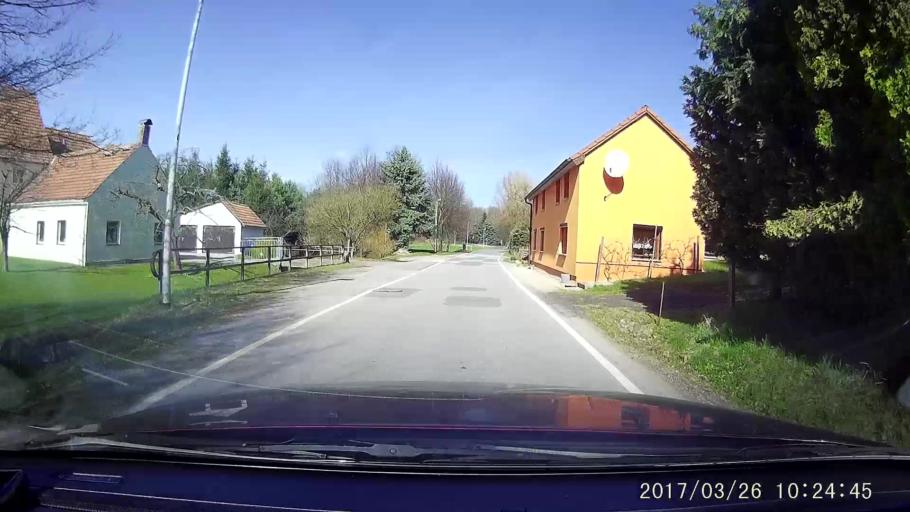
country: DE
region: Saxony
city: Sohland am Rotstein
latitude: 51.1042
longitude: 14.7367
